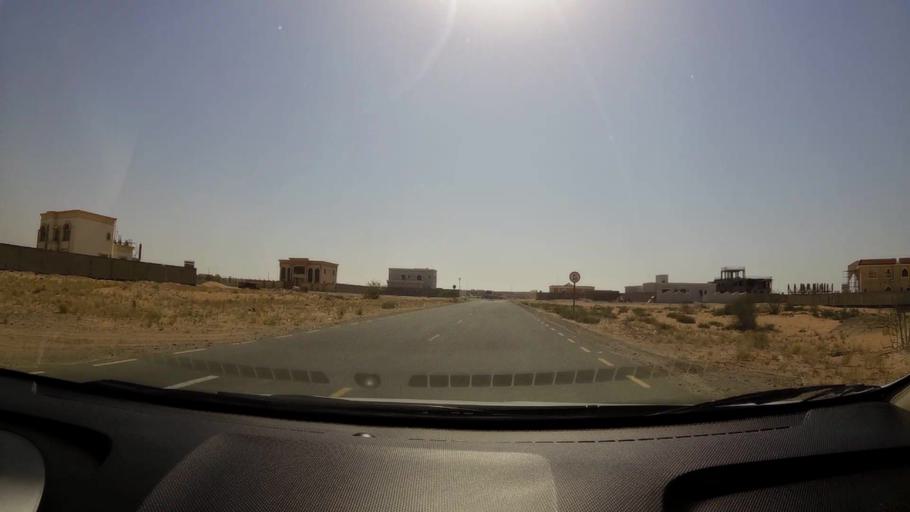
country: AE
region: Umm al Qaywayn
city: Umm al Qaywayn
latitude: 25.4768
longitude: 55.6089
